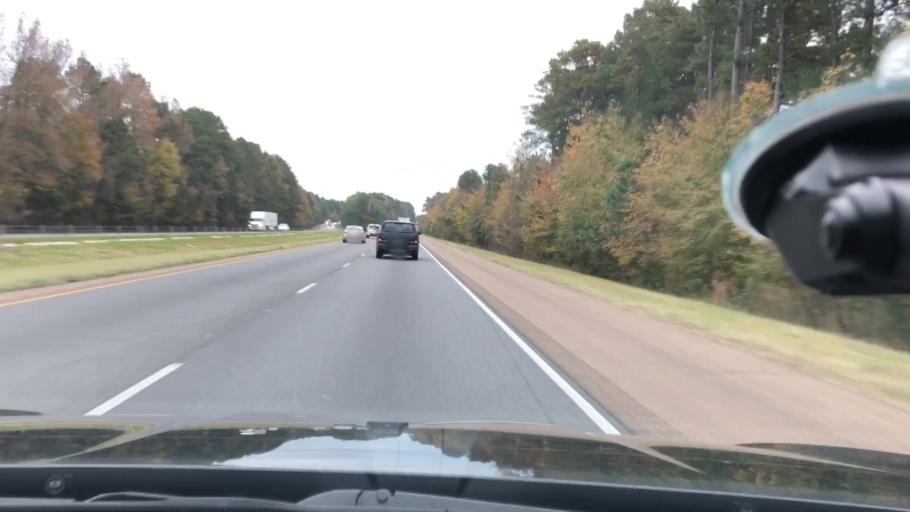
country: US
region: Arkansas
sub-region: Clark County
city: Gurdon
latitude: 33.9142
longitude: -93.2819
